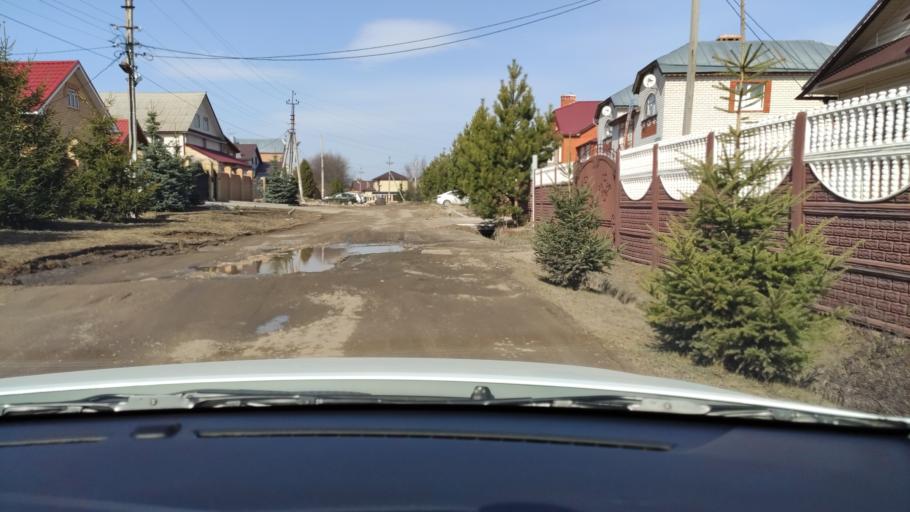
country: RU
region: Tatarstan
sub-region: Gorod Kazan'
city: Kazan
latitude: 55.7857
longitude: 49.2477
